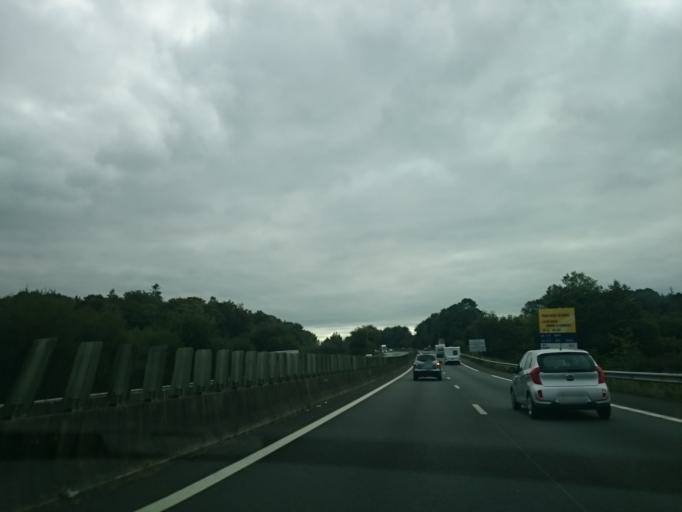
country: FR
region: Brittany
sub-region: Departement du Morbihan
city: Plougoumelen
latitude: 47.6683
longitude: -2.9200
